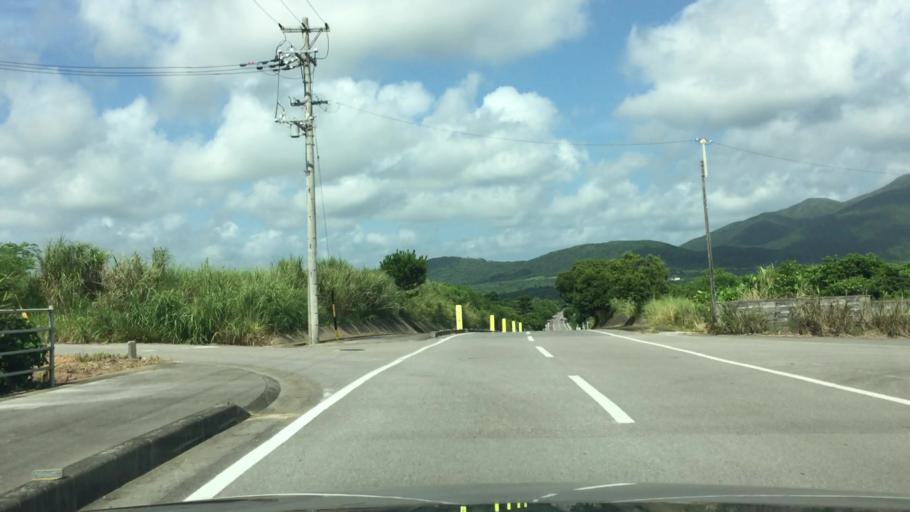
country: JP
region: Okinawa
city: Ishigaki
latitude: 24.4104
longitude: 124.2269
